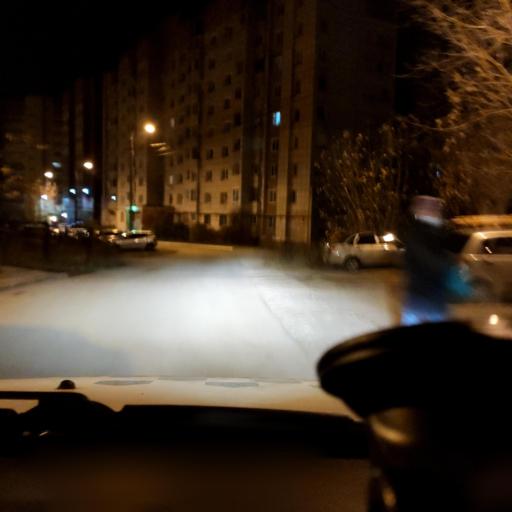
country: RU
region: Perm
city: Perm
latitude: 58.0986
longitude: 56.2990
